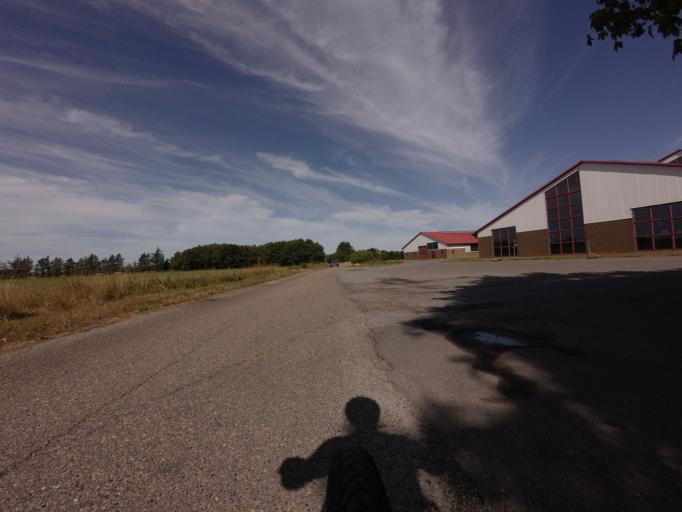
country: DK
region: North Denmark
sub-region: Hjorring Kommune
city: Vra
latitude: 57.4000
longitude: 9.9498
